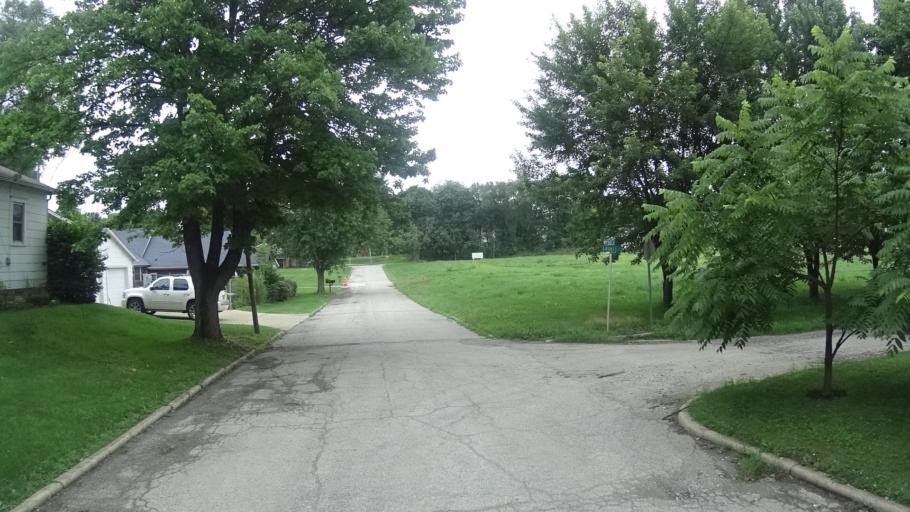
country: US
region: Indiana
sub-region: Madison County
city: Pendleton
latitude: 39.9986
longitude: -85.7489
